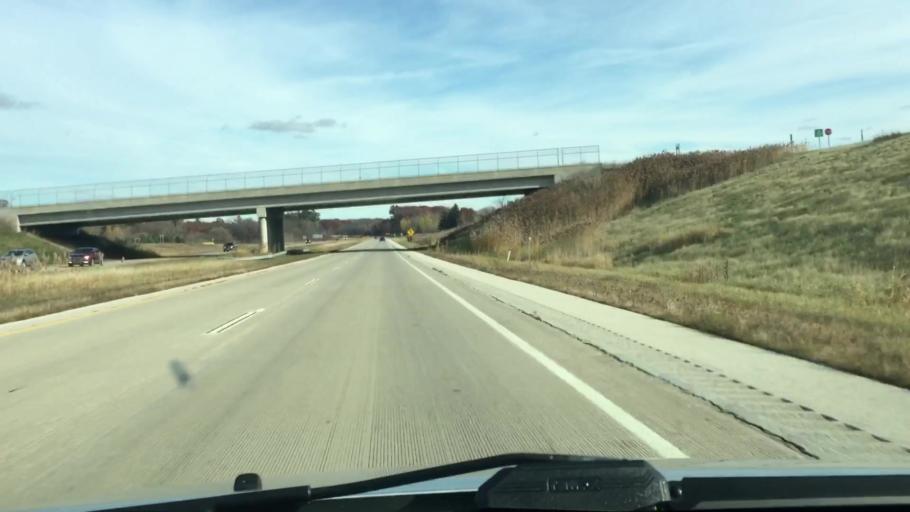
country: US
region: Wisconsin
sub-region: Kewaunee County
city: Luxemburg
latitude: 44.6338
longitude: -87.7770
